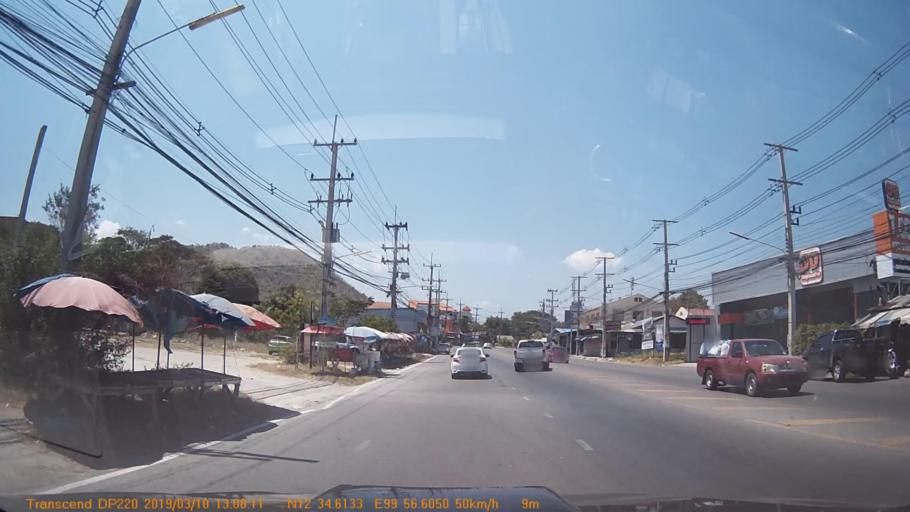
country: TH
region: Prachuap Khiri Khan
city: Hua Hin
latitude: 12.5769
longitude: 99.9433
